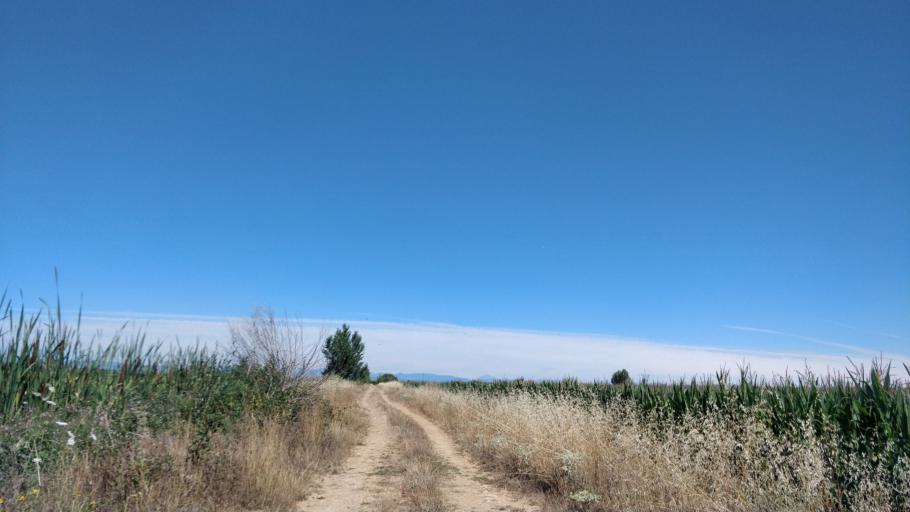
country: ES
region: Castille and Leon
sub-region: Provincia de Leon
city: Bustillo del Paramo
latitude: 42.4484
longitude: -5.8159
